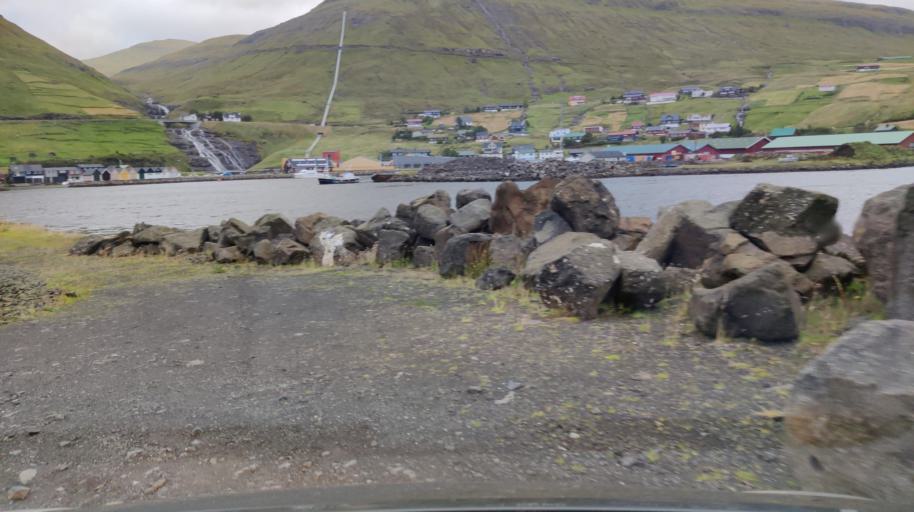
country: FO
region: Streymoy
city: Vestmanna
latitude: 62.1504
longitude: -7.1532
